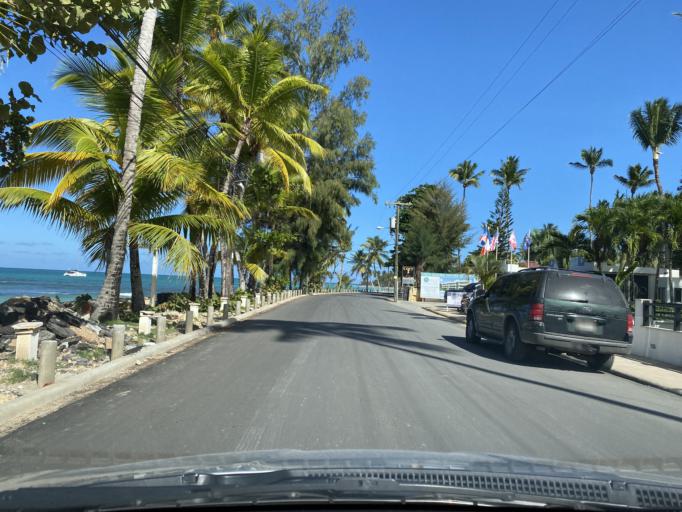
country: DO
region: Samana
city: Las Terrenas
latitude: 19.3228
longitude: -69.5348
